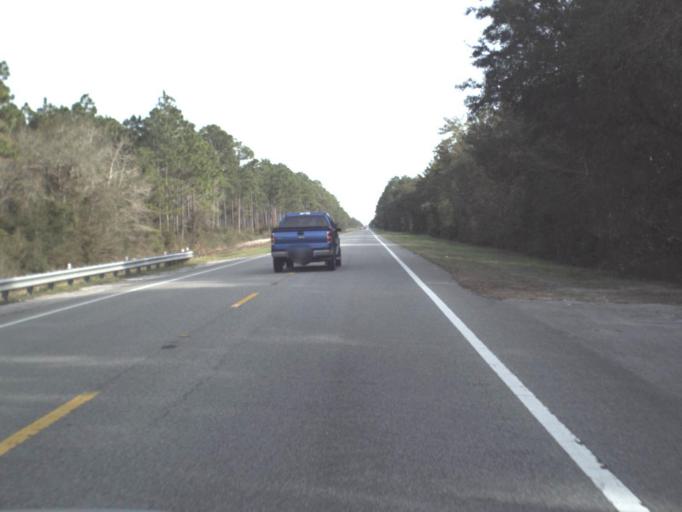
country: US
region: Florida
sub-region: Bay County
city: Mexico Beach
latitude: 29.9710
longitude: -85.4575
